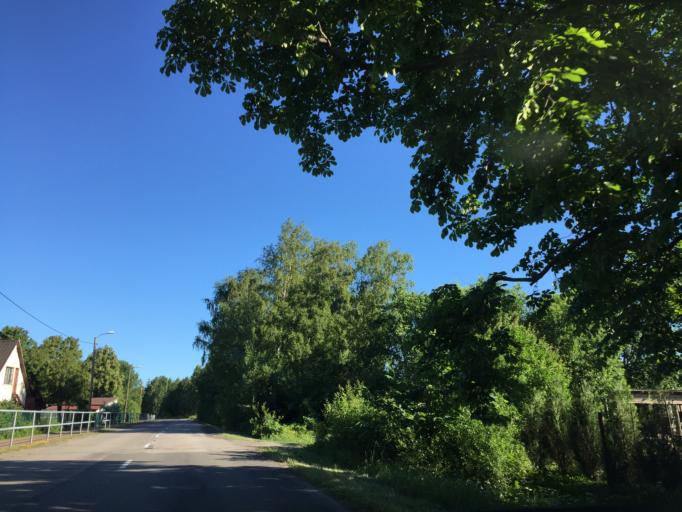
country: LV
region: Ventspils
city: Ventspils
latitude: 57.4364
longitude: 21.6232
